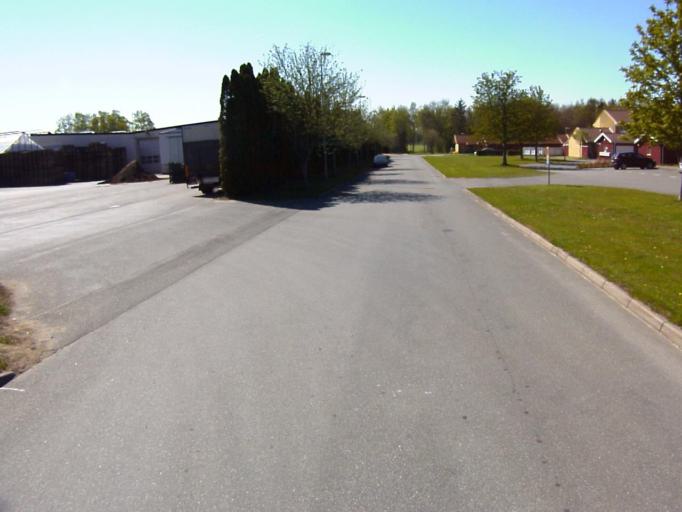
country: SE
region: Skane
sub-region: Kristianstads Kommun
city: Kristianstad
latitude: 56.0308
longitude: 14.1949
